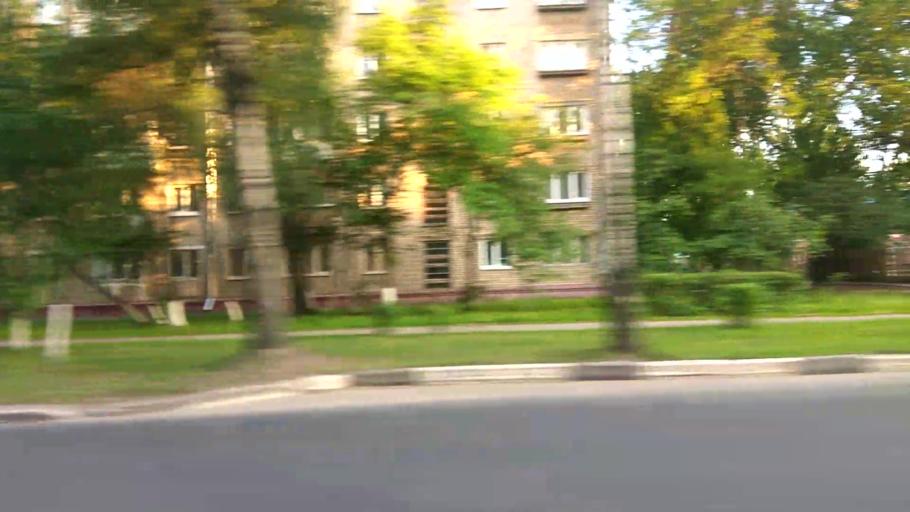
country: RU
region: Moskovskaya
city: Korolev
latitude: 55.9132
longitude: 37.8223
